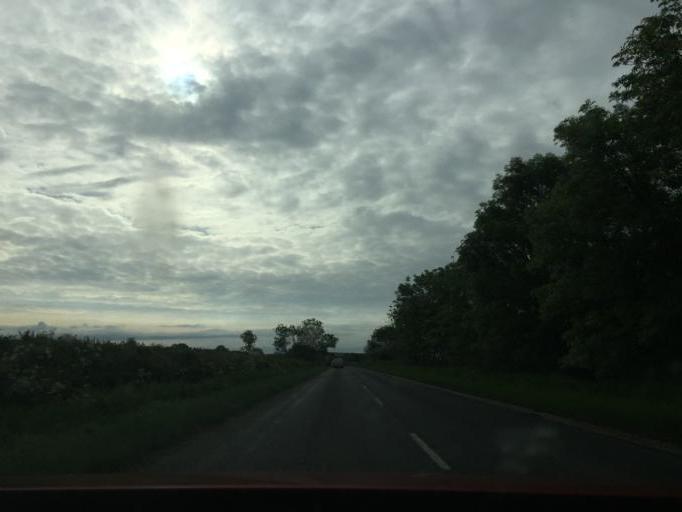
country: GB
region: England
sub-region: Leicestershire
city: Lutterworth
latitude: 52.4522
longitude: -1.2621
